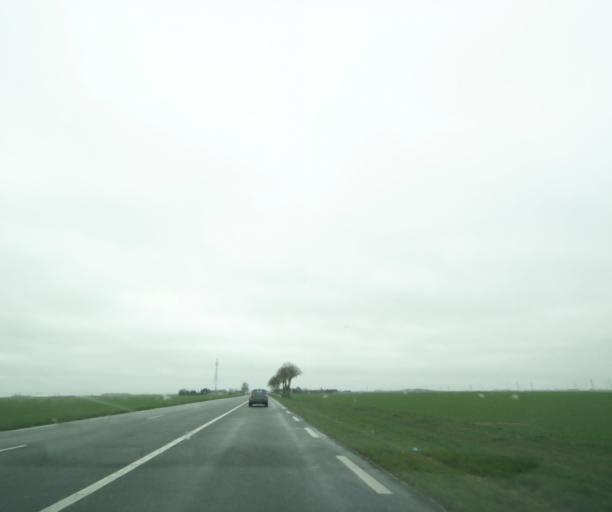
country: FR
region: Centre
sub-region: Departement d'Eure-et-Loir
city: Toury
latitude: 48.2337
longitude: 1.9534
